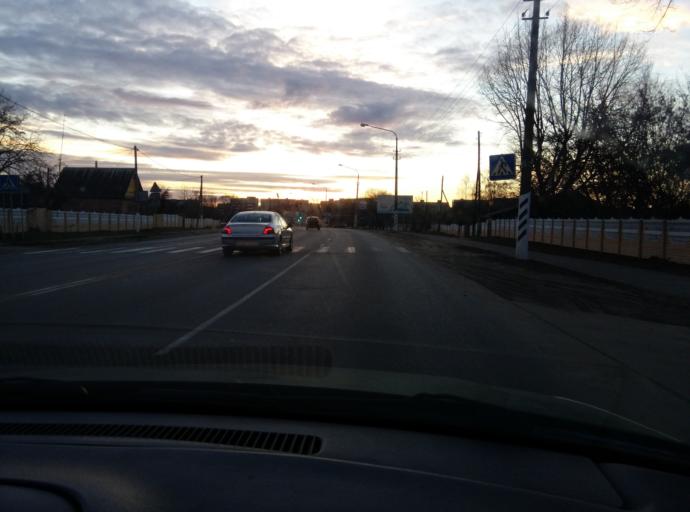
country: BY
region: Minsk
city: Horad Barysaw
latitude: 54.2275
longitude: 28.4977
